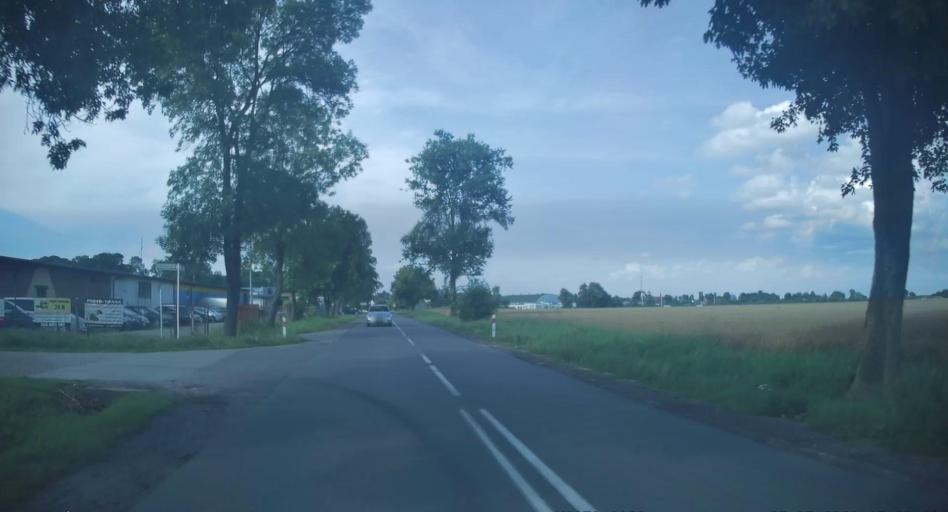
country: PL
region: Lodz Voivodeship
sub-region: Powiat tomaszowski
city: Rzeczyca
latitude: 51.5939
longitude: 20.2911
